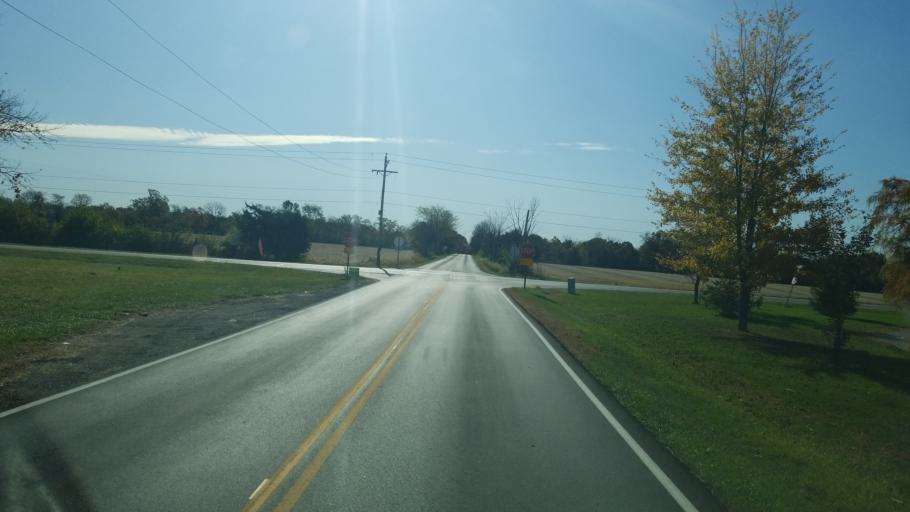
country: US
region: Ohio
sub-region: Warren County
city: Morrow
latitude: 39.3705
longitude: -84.0646
